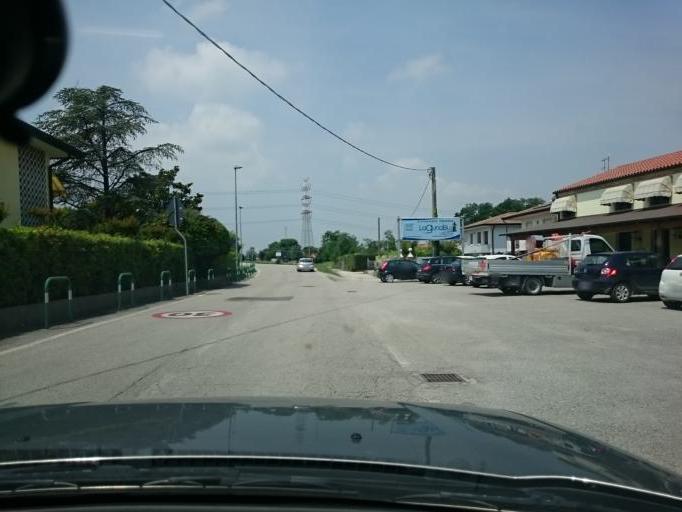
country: IT
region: Veneto
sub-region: Provincia di Padova
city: Codevigo
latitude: 45.2455
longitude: 12.1330
